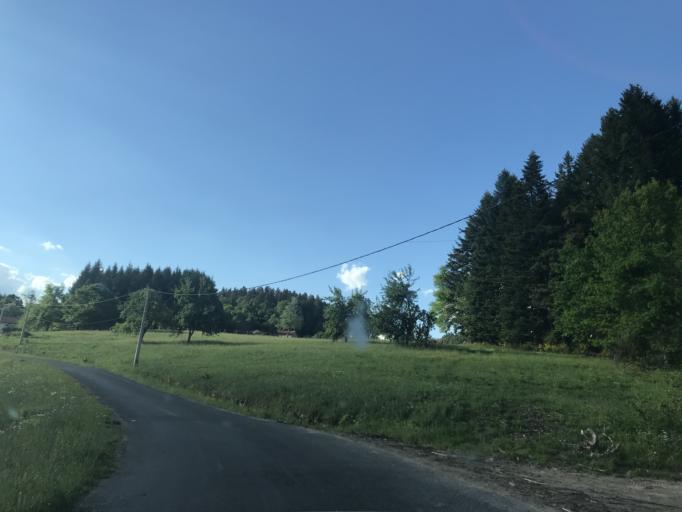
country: FR
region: Auvergne
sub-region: Departement du Puy-de-Dome
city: Job
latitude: 45.7098
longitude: 3.7011
